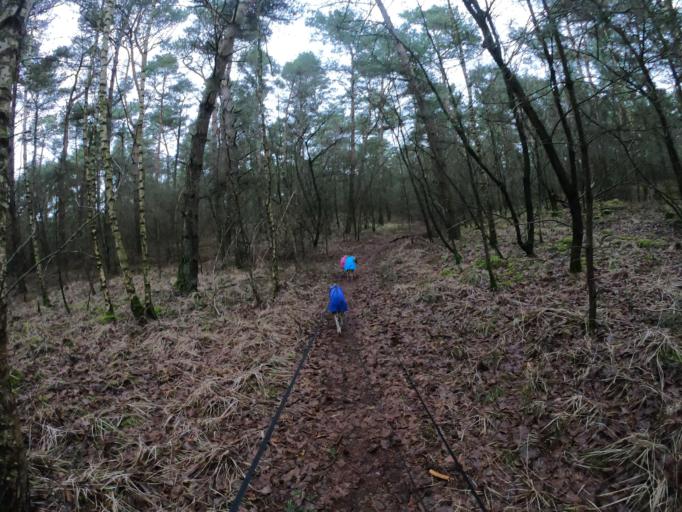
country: BE
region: Flanders
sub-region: Provincie Antwerpen
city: Stabroek
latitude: 51.3608
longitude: 4.3606
